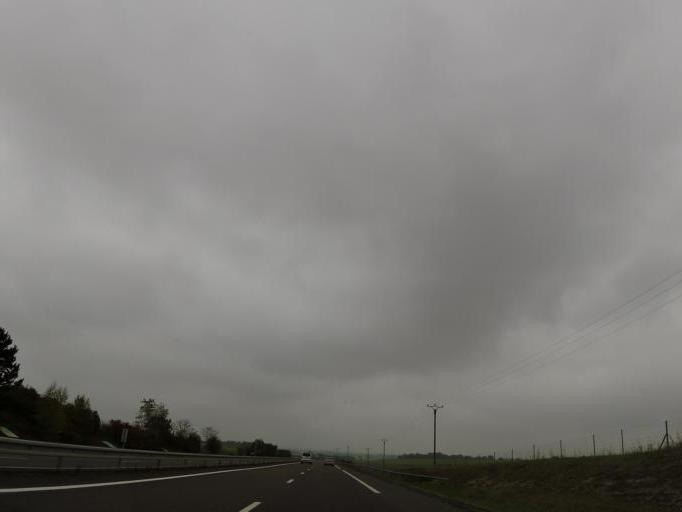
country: FR
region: Champagne-Ardenne
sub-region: Departement de la Marne
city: Sainte-Menehould
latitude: 49.0695
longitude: 4.7547
